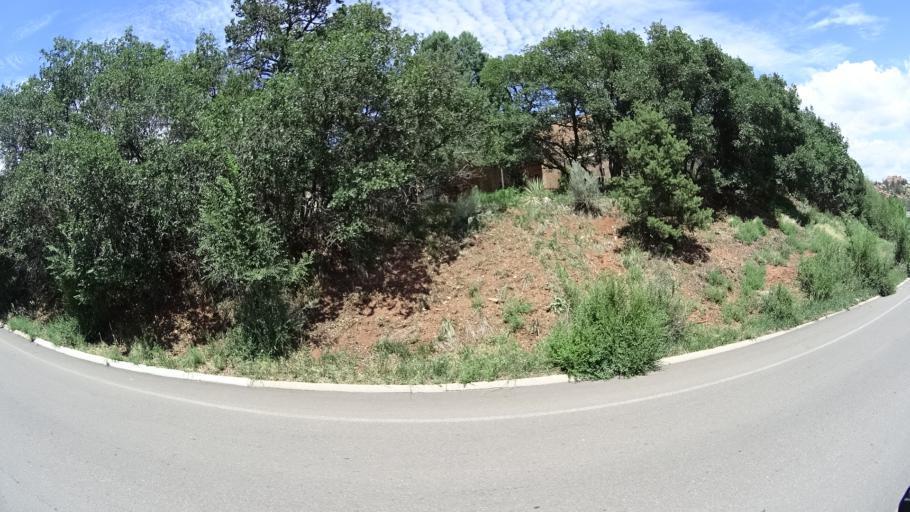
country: US
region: Colorado
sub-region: El Paso County
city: Manitou Springs
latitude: 38.8579
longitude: -104.8987
